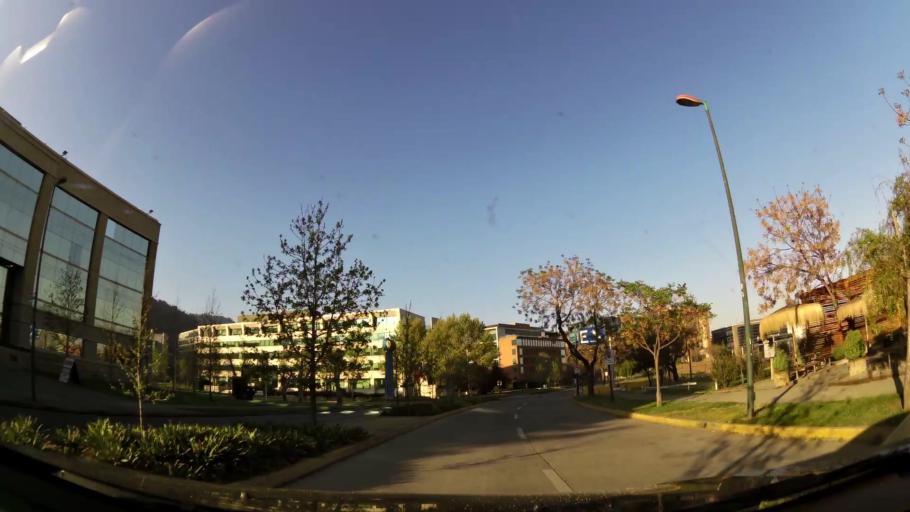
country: CL
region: Santiago Metropolitan
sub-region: Provincia de Santiago
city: Santiago
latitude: -33.3917
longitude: -70.6153
